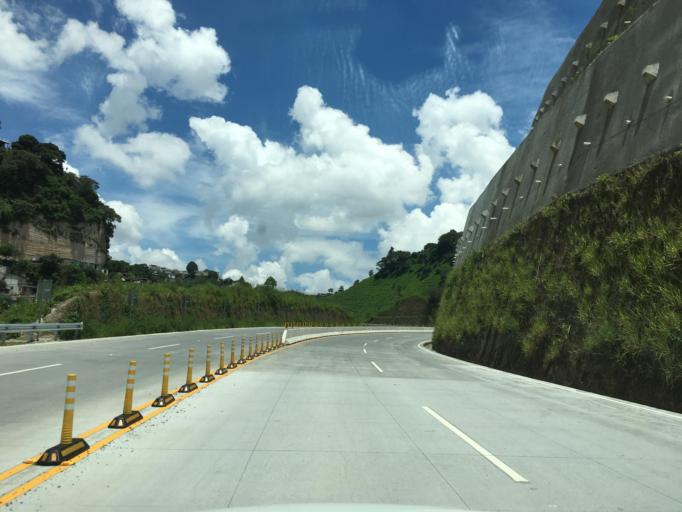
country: GT
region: Guatemala
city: Santa Catarina Pinula
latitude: 14.5537
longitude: -90.5329
